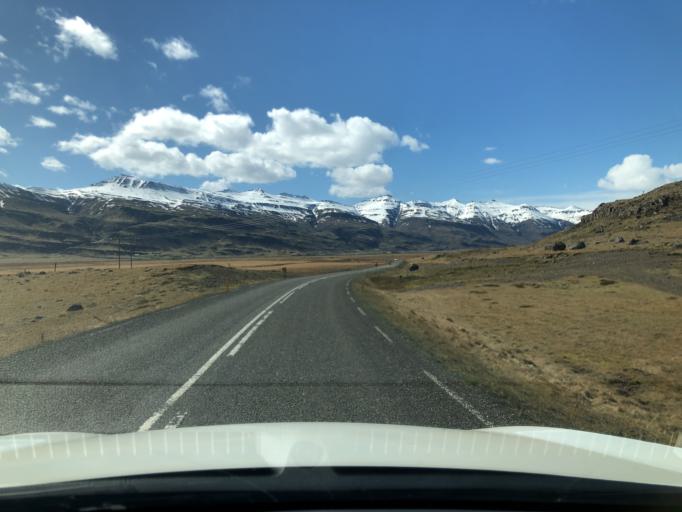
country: IS
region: East
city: Reydarfjoerdur
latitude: 64.5678
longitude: -14.5889
